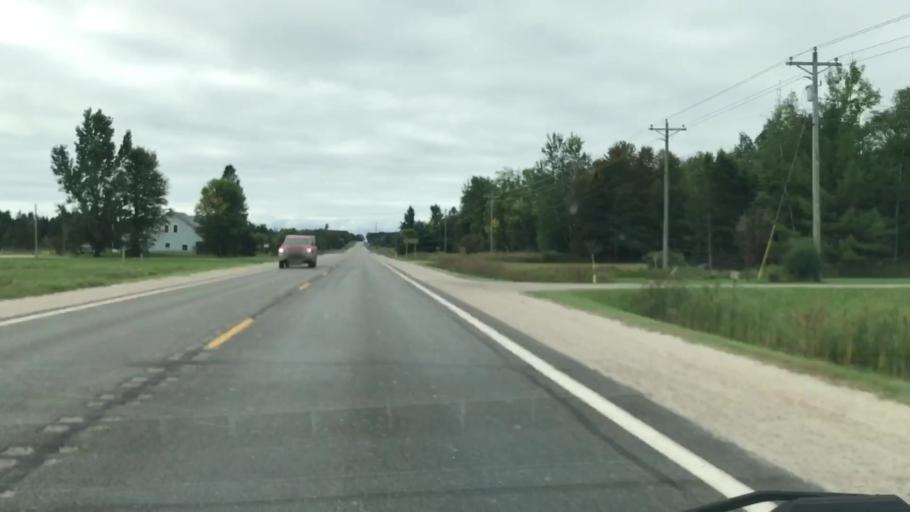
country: US
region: Michigan
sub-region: Luce County
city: Newberry
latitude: 46.1387
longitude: -85.5714
